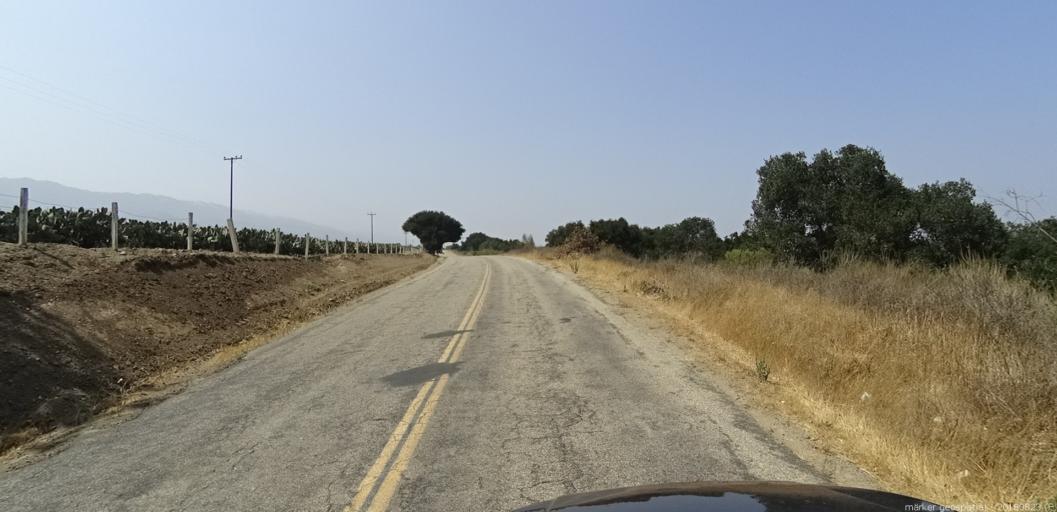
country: US
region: California
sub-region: Monterey County
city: Gonzales
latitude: 36.4488
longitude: -121.4350
